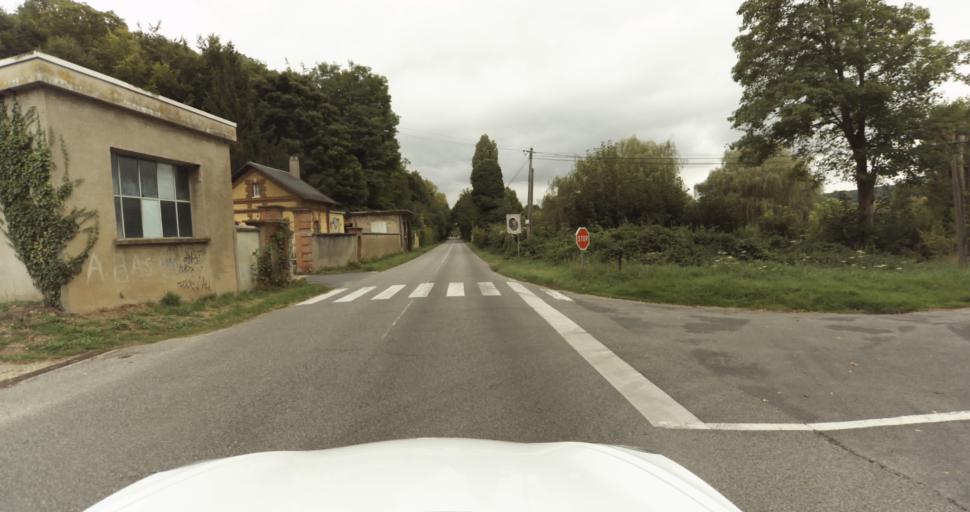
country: FR
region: Haute-Normandie
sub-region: Departement de l'Eure
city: Saint-Sebastien-de-Morsent
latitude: 48.9983
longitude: 1.0737
